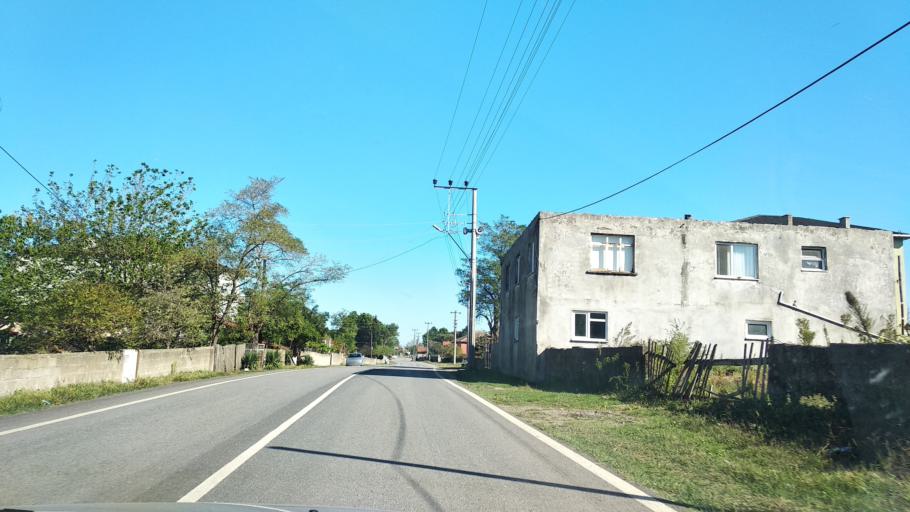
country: TR
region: Sakarya
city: Karasu
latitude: 41.1181
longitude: 30.6250
